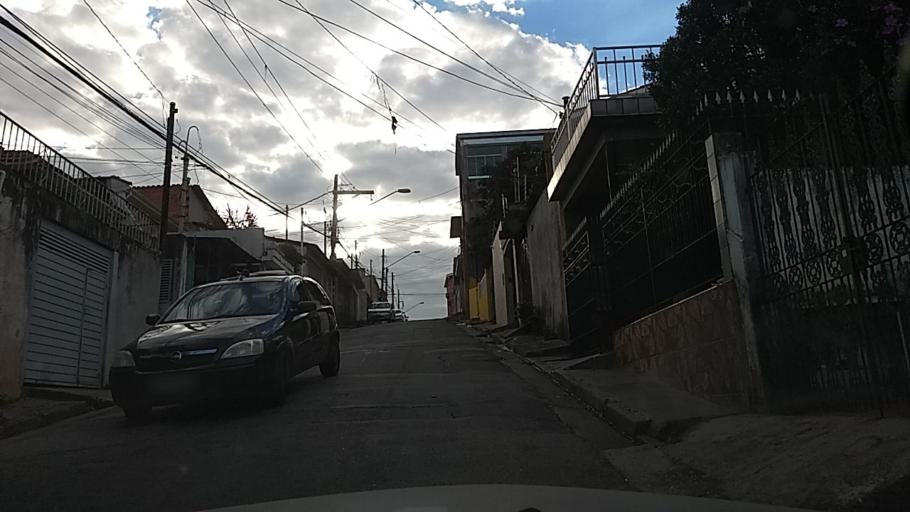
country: BR
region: Sao Paulo
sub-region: Guarulhos
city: Guarulhos
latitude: -23.4903
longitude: -46.5923
